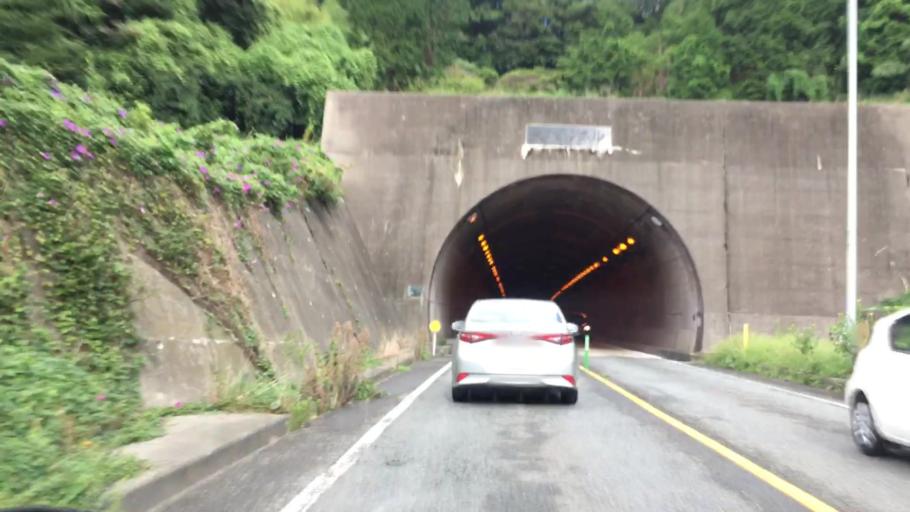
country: JP
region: Fukuoka
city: Maebaru-chuo
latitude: 33.5043
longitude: 130.1067
